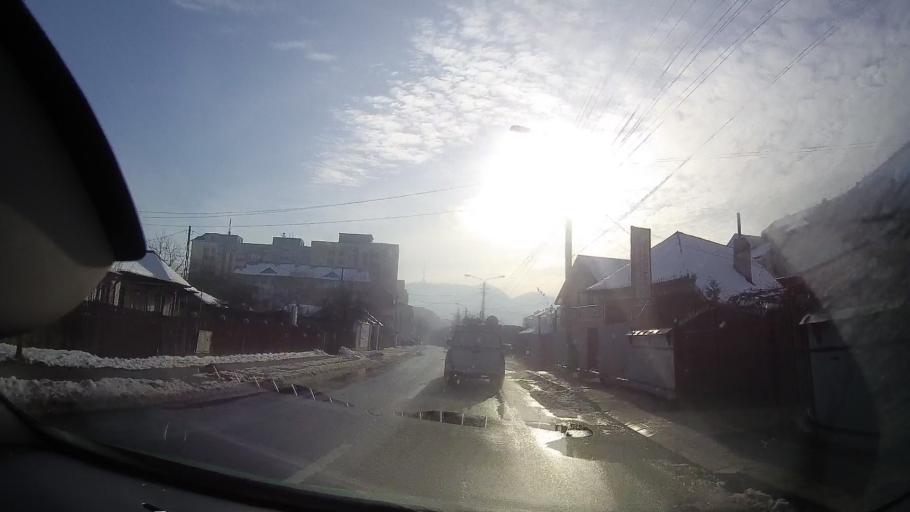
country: RO
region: Neamt
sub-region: Municipiul Piatra-Neamt
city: Valeni
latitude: 46.9443
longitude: 26.3827
